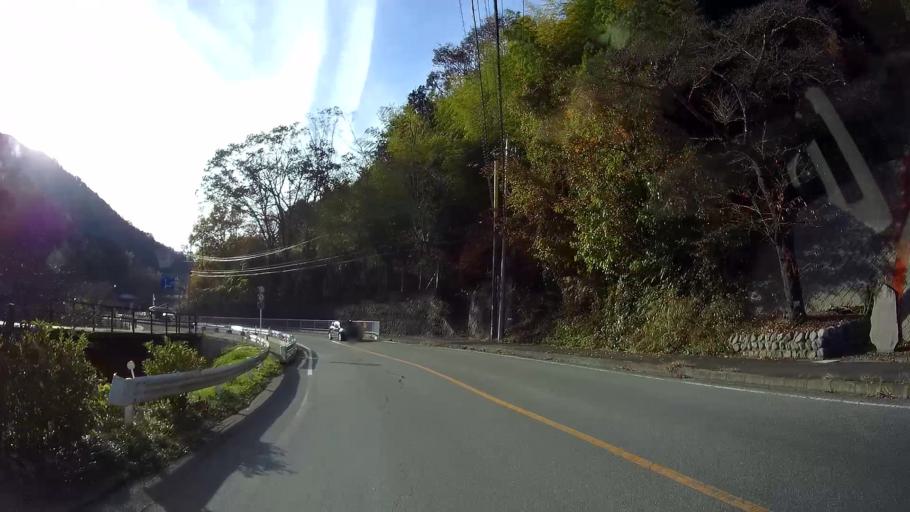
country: JP
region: Yamanashi
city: Fujikawaguchiko
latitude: 35.4747
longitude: 138.5361
